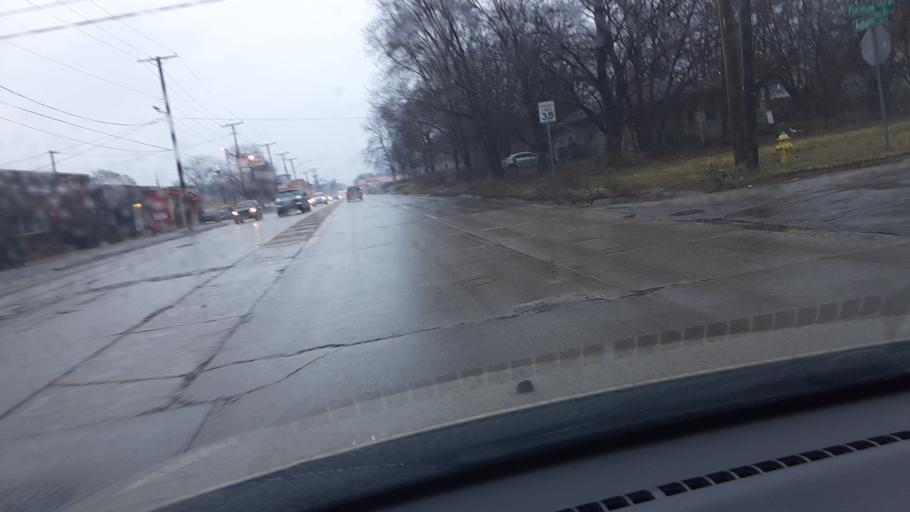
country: US
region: Illinois
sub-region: Winnebago County
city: Rockford
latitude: 42.2883
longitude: -89.1120
